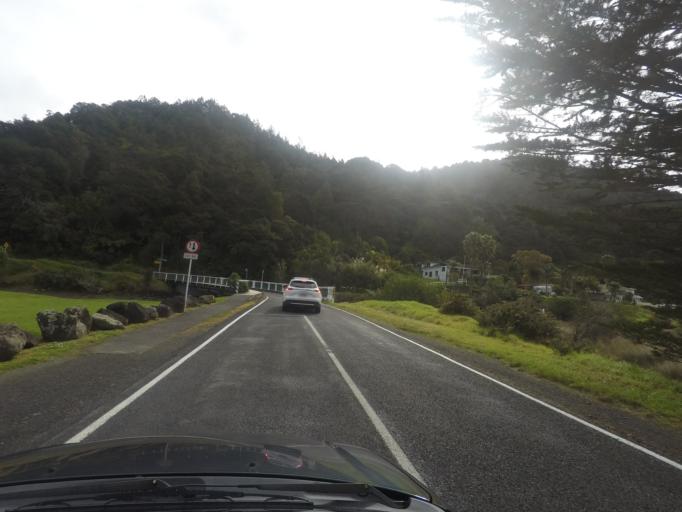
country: NZ
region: Auckland
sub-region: Auckland
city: Titirangi
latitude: -36.9984
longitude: 174.5672
